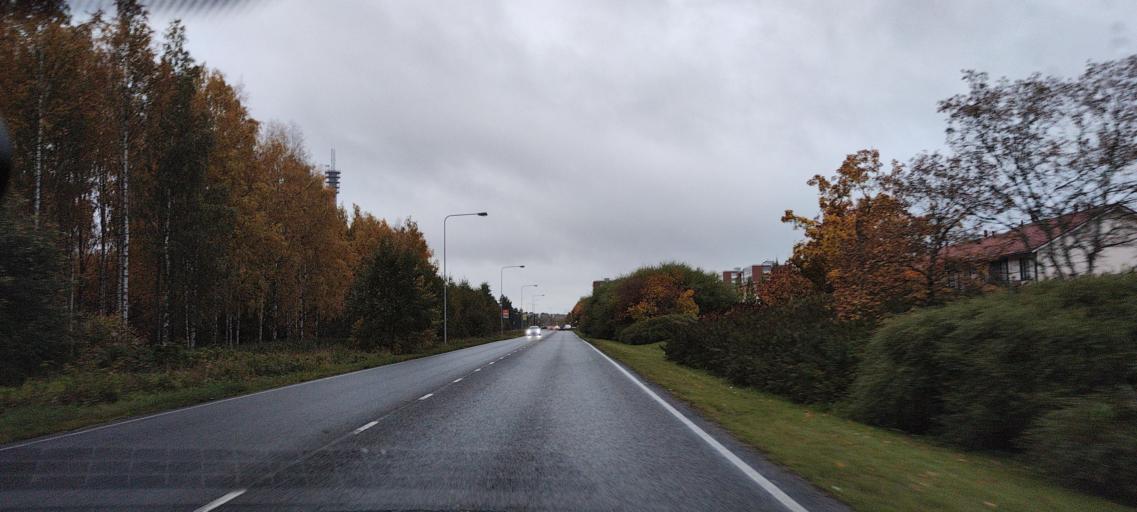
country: FI
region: Varsinais-Suomi
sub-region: Turku
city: Kaarina
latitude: 60.4537
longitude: 22.3325
